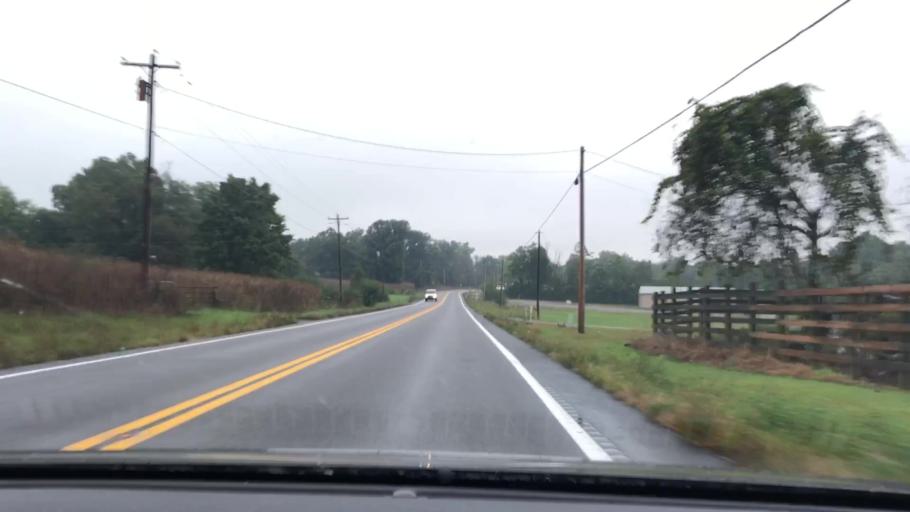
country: US
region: Tennessee
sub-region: Fentress County
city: Grimsley
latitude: 36.1847
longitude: -85.0326
